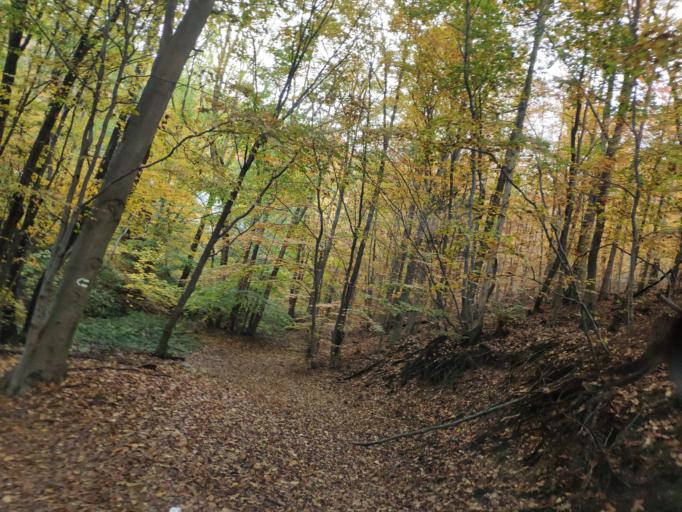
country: SK
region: Kosicky
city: Moldava nad Bodvou
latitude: 48.7197
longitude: 21.0108
